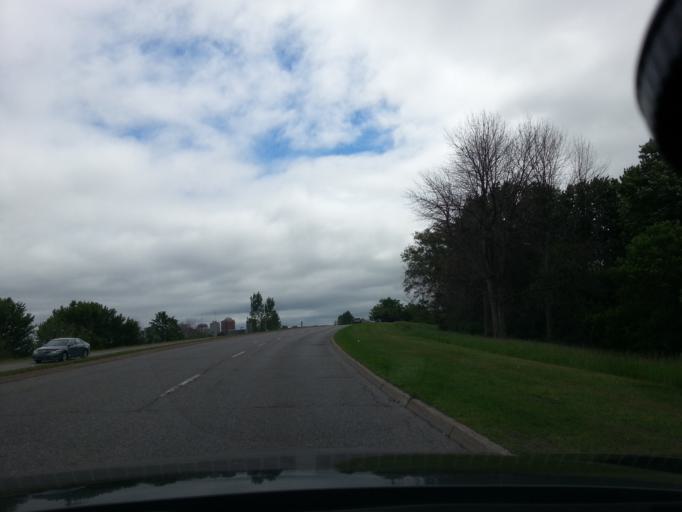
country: CA
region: Ontario
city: Ottawa
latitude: 45.4109
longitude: -75.7275
